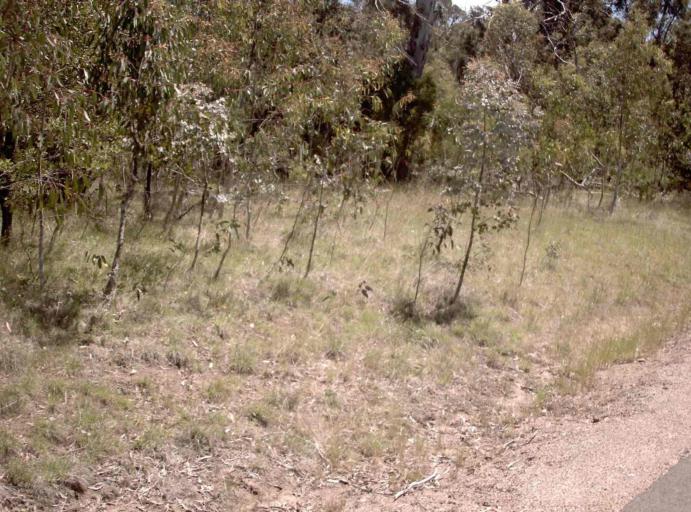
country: AU
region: New South Wales
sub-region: Snowy River
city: Jindabyne
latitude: -37.1117
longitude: 148.2503
